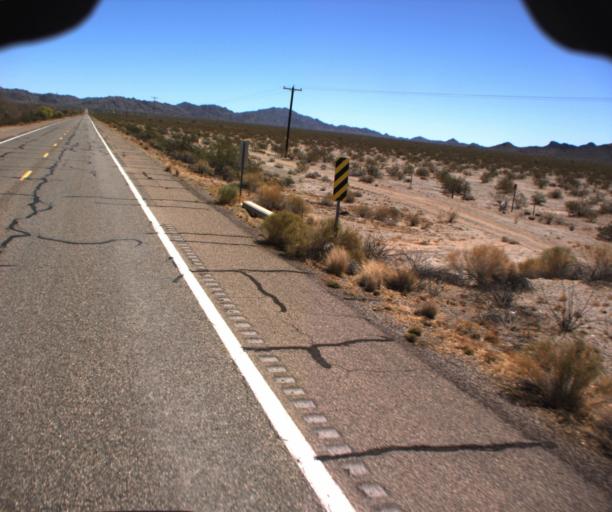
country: US
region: Arizona
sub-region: La Paz County
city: Salome
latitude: 33.7206
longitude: -113.7387
